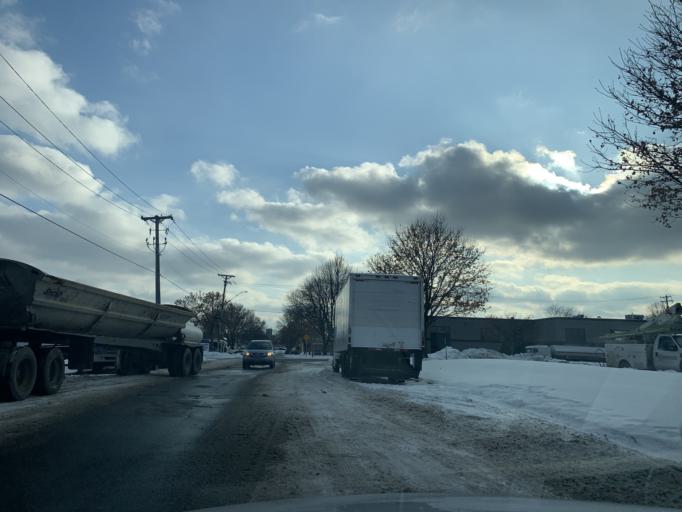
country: US
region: Minnesota
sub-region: Hennepin County
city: Minneapolis
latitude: 44.9920
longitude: -93.2894
